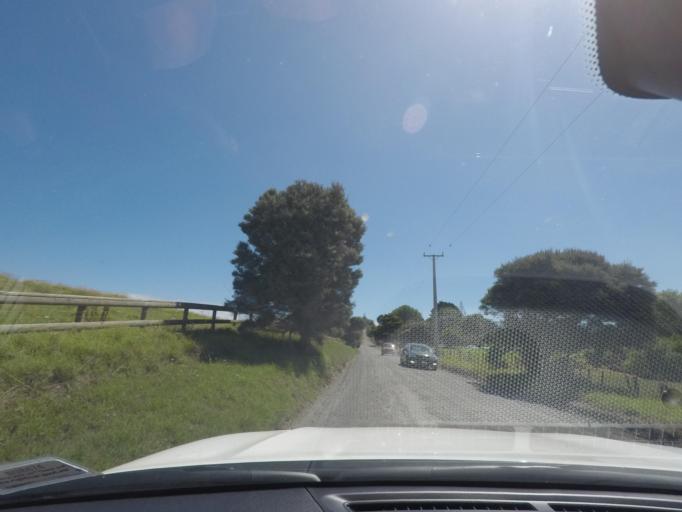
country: NZ
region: Auckland
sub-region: Auckland
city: Parakai
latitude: -36.5796
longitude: 174.3223
